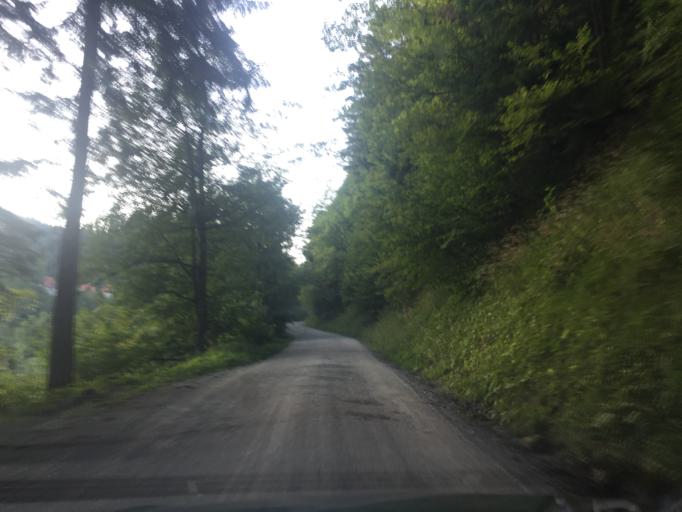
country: SI
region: Ravne na Koroskem
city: Kotlje
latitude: 46.4561
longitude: 14.9829
